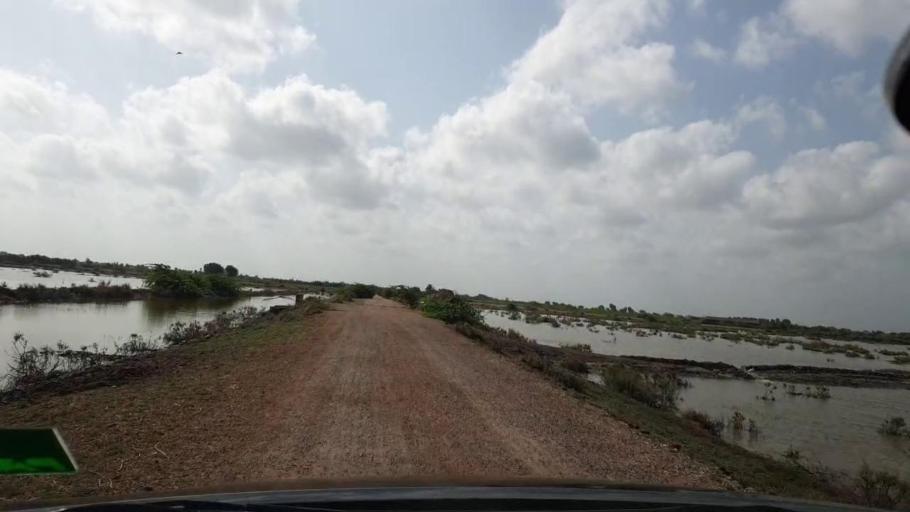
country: PK
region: Sindh
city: Kadhan
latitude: 24.6357
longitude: 69.0888
